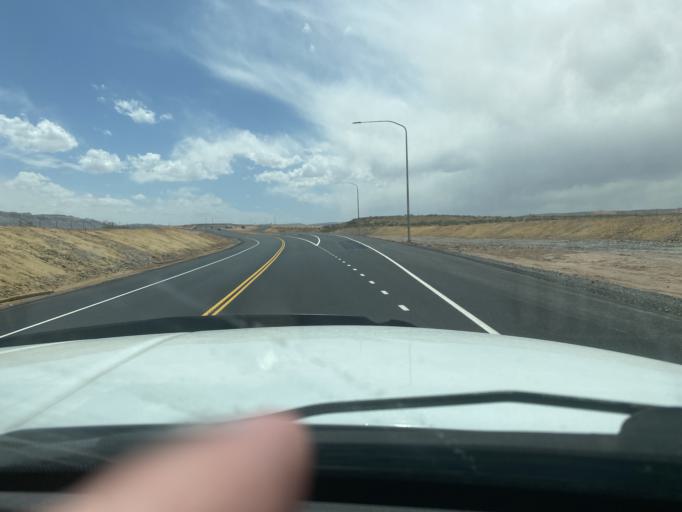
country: US
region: Utah
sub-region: Washington County
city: Hurricane
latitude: 37.1344
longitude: -113.3479
